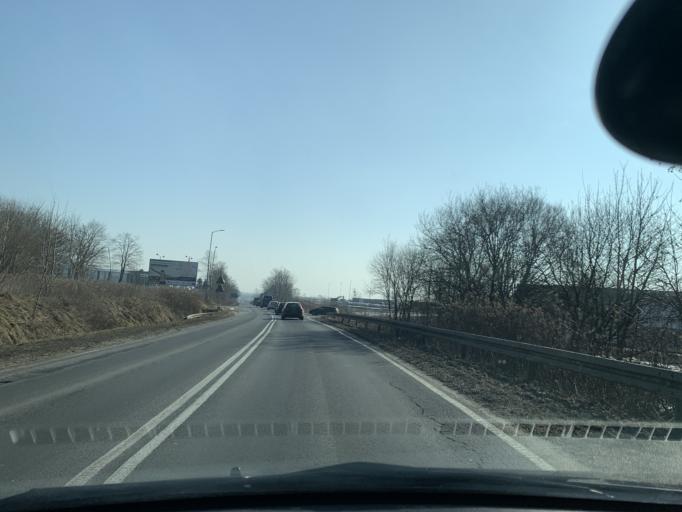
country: PL
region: Silesian Voivodeship
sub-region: Piekary Slaskie
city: Piekary Slaskie
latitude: 50.3795
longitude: 18.9266
